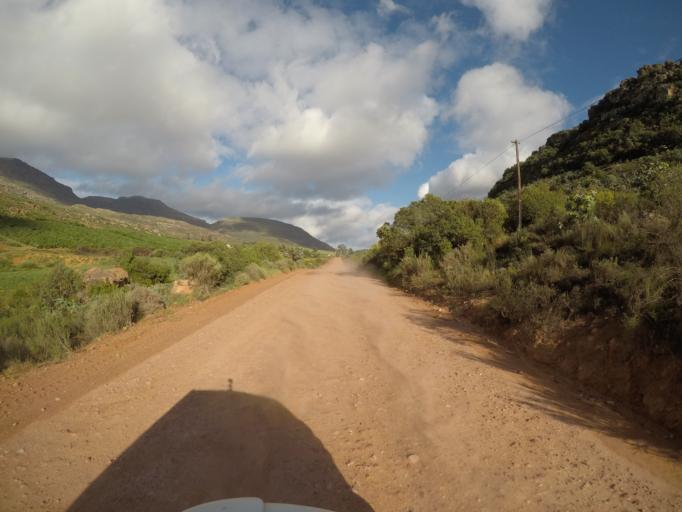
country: ZA
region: Western Cape
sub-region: West Coast District Municipality
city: Clanwilliam
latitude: -32.3435
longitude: 18.8173
